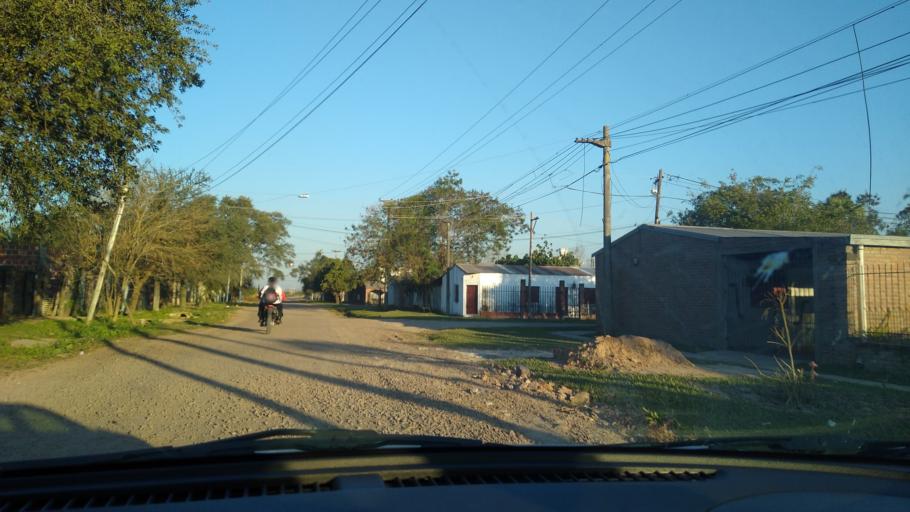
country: AR
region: Chaco
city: Puerto Vilelas
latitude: -27.5023
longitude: -58.9575
